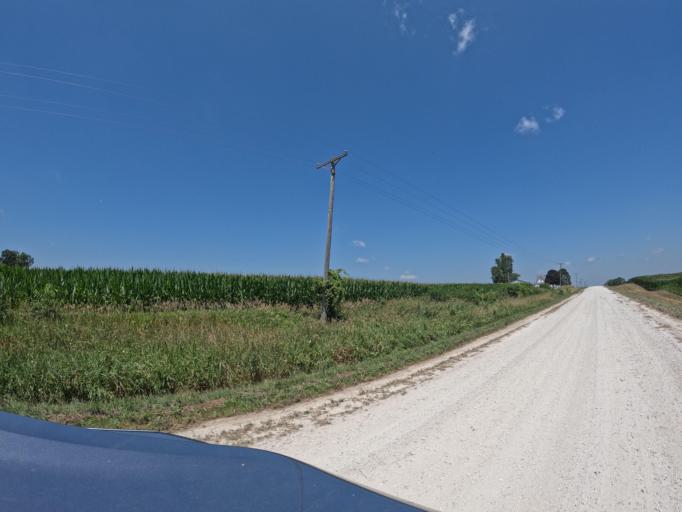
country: US
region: Iowa
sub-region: Keokuk County
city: Sigourney
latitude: 41.2658
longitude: -92.2381
